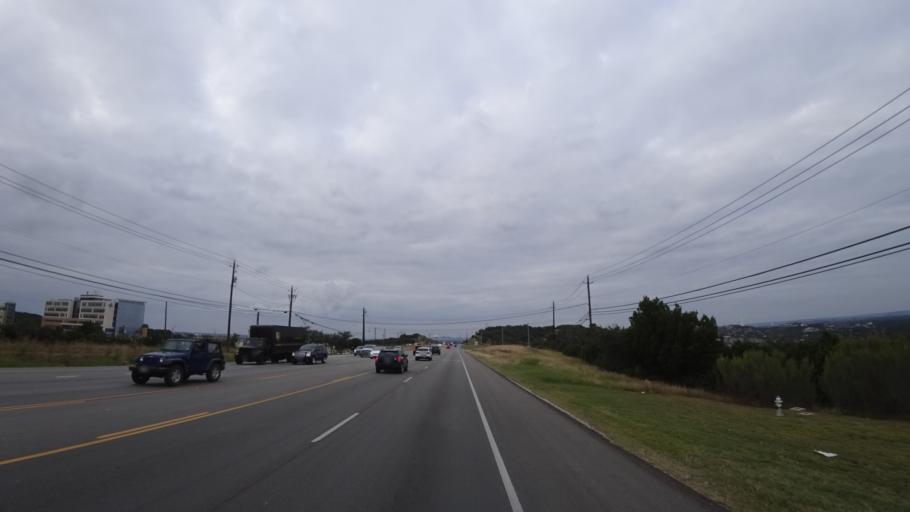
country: US
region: Texas
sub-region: Travis County
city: The Hills
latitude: 30.3318
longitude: -97.9676
